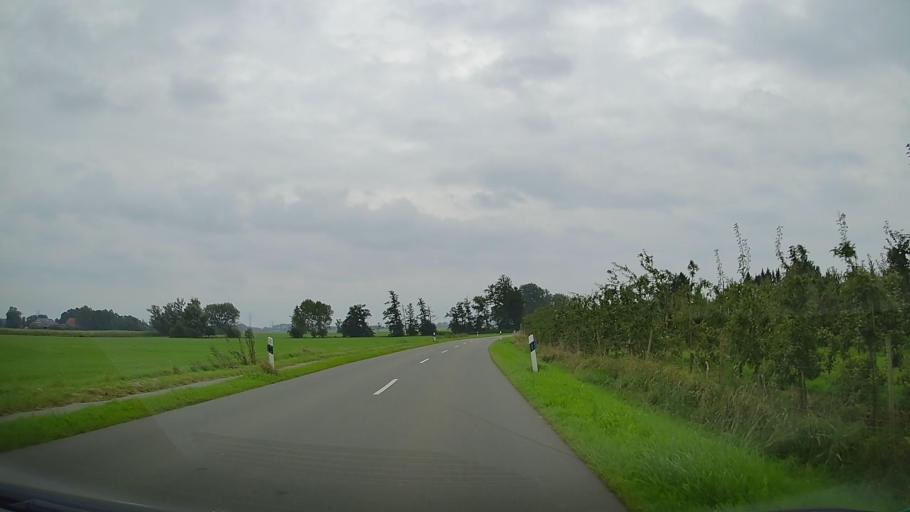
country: DE
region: Lower Saxony
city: Stade
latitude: 53.6304
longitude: 9.4657
